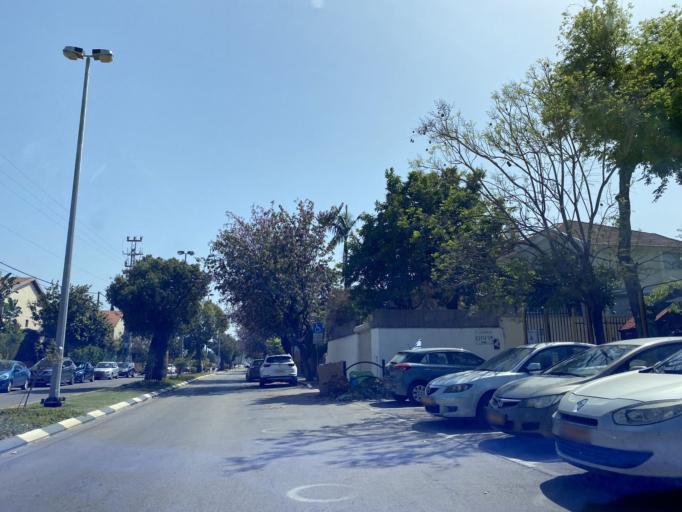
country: IL
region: Central District
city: Ra'anana
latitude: 32.1762
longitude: 34.8804
